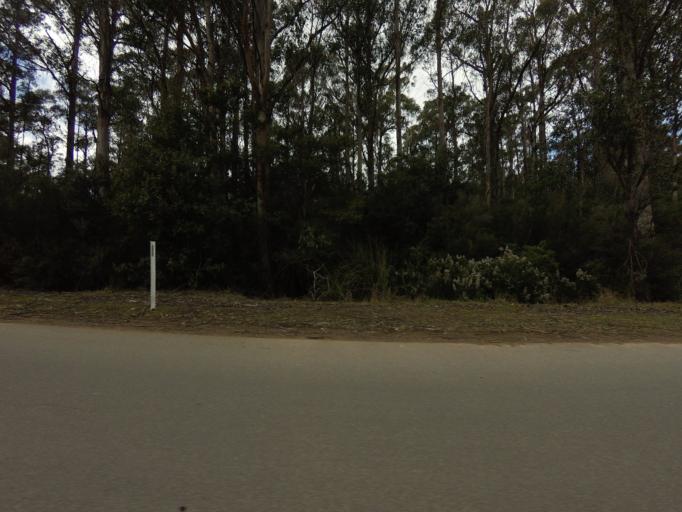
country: AU
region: Tasmania
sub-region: Huon Valley
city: Geeveston
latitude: -43.3645
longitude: 146.9592
